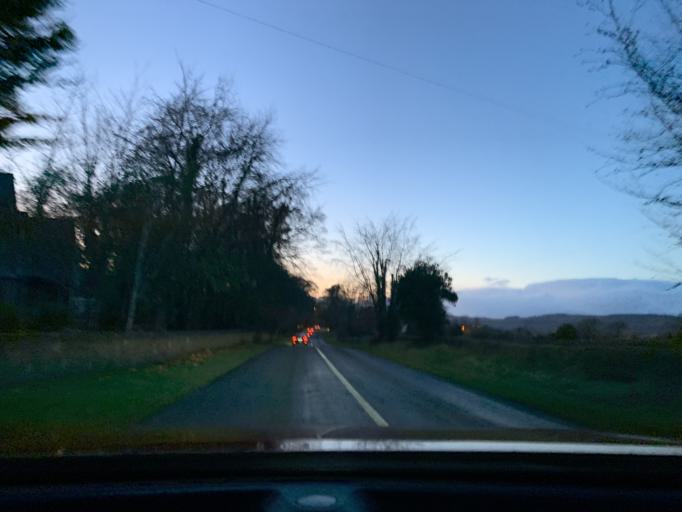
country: IE
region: Connaught
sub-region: Roscommon
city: Boyle
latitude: 53.9685
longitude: -8.2690
